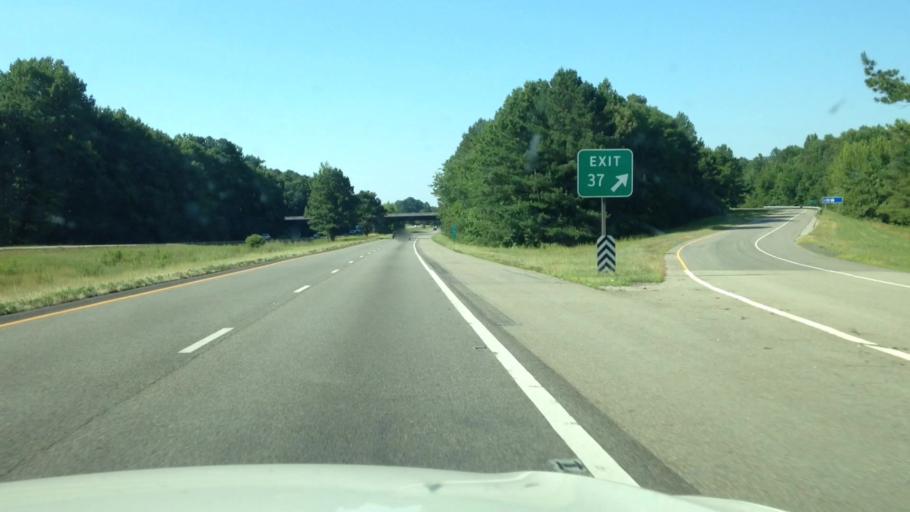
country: US
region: Virginia
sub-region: Sussex County
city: Sussex
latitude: 37.0314
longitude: -77.3907
